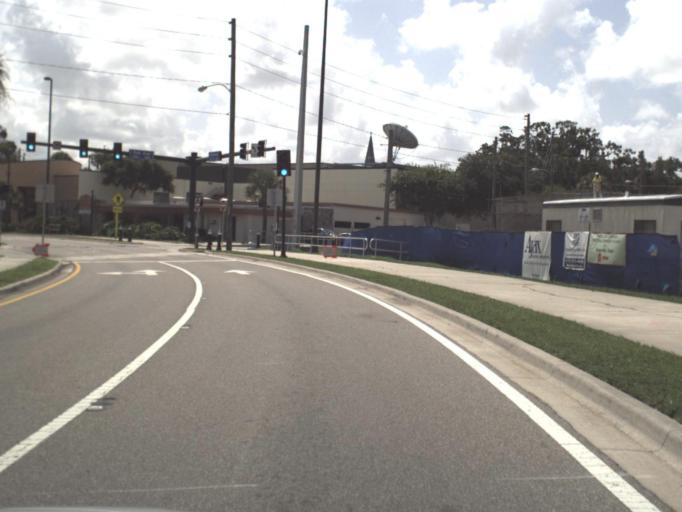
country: US
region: Florida
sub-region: Pinellas County
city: Clearwater
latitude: 27.9614
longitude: -82.8022
